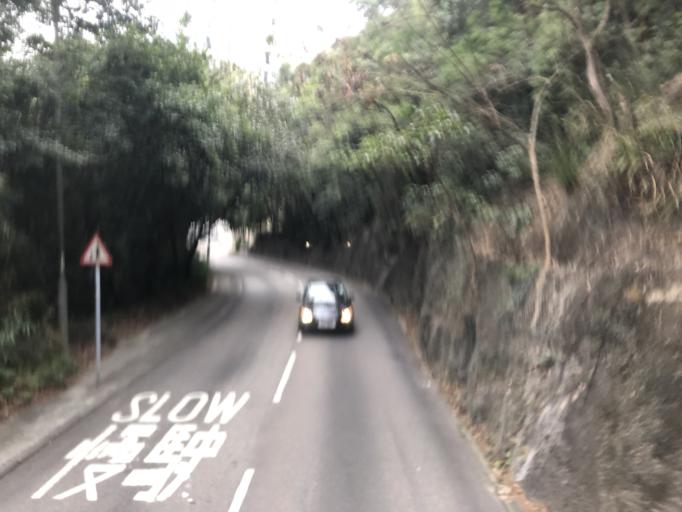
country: HK
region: Wanchai
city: Wan Chai
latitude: 22.2684
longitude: 114.1736
